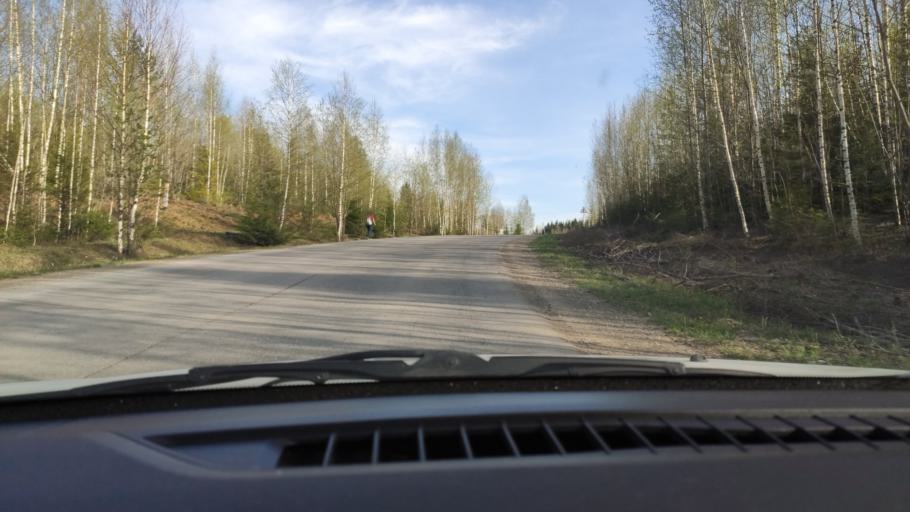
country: RU
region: Perm
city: Novyye Lyady
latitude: 57.9274
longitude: 56.6506
